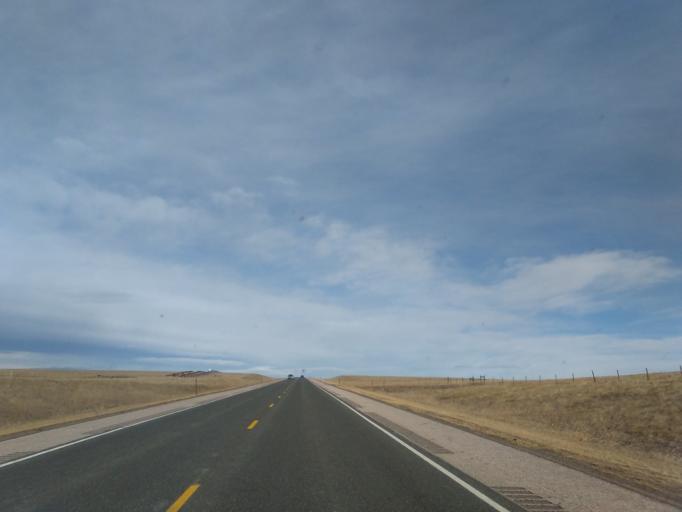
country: US
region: Wyoming
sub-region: Laramie County
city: Pine Bluffs
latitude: 41.5883
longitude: -104.2684
